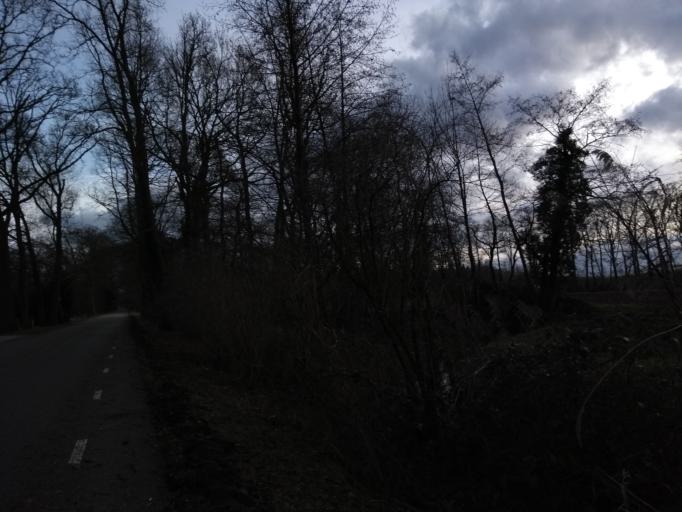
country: NL
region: Overijssel
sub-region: Gemeente Enschede
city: Enschede
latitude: 52.2528
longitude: 6.8834
